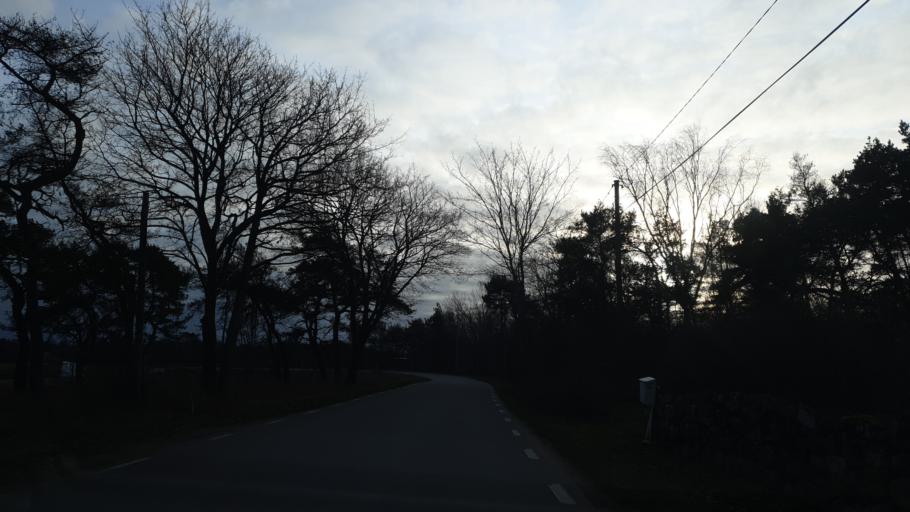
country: SE
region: Kalmar
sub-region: Torsas Kommun
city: Torsas
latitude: 56.2668
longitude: 16.0318
